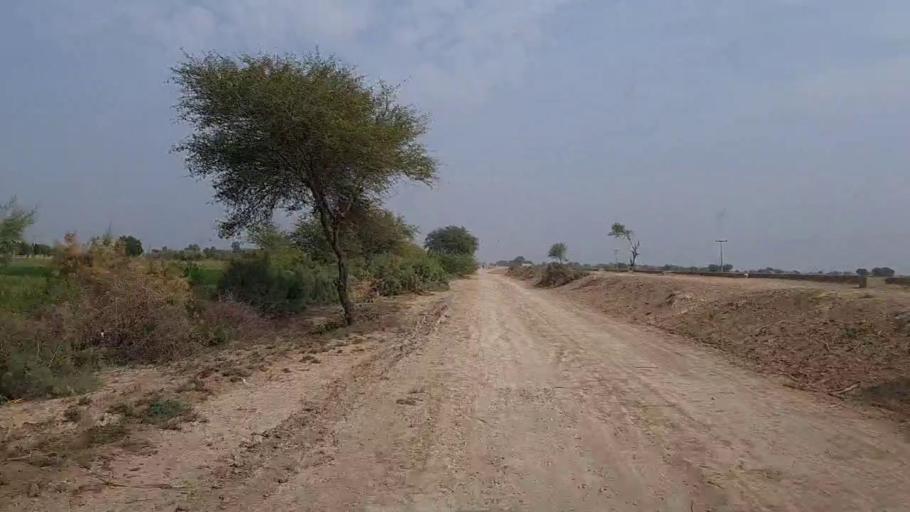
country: PK
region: Sindh
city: Mirwah Gorchani
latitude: 25.3979
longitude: 69.1004
